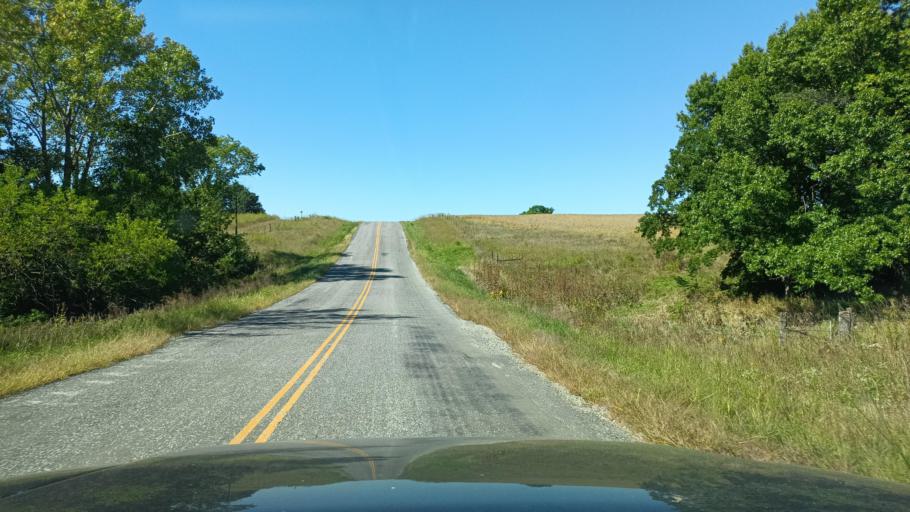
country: US
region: Missouri
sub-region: Adair County
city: Kirksville
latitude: 40.3301
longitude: -92.5410
